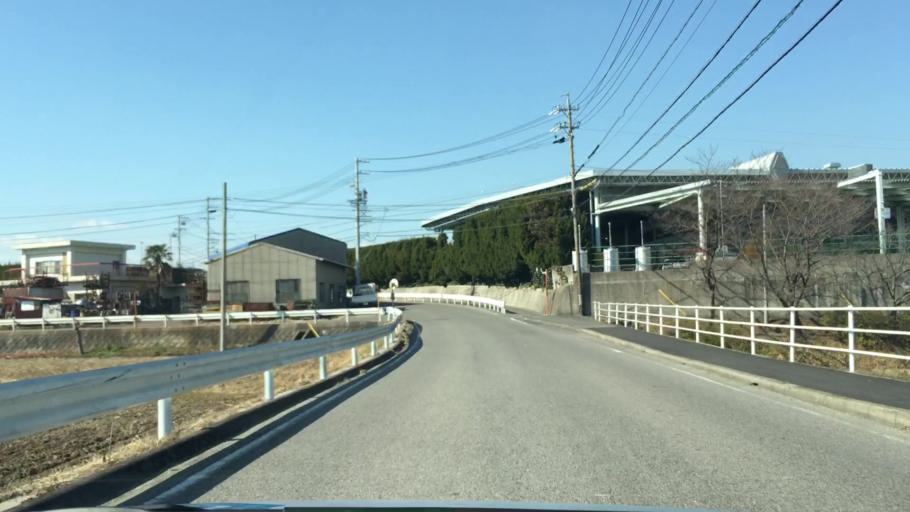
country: JP
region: Aichi
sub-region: Toyota-shi
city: Toyota
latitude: 35.0333
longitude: 137.1274
